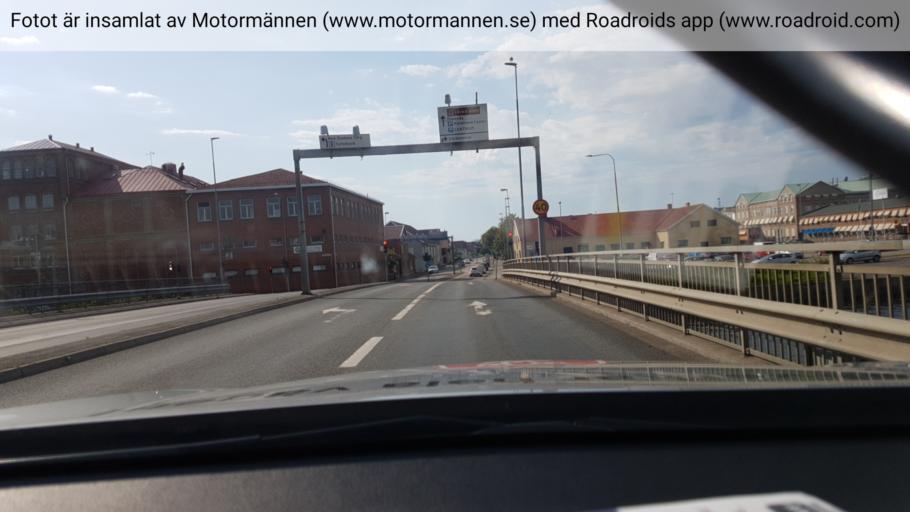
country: SE
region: Vaestra Goetaland
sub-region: Lidkopings Kommun
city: Lidkoping
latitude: 58.5046
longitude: 13.1617
